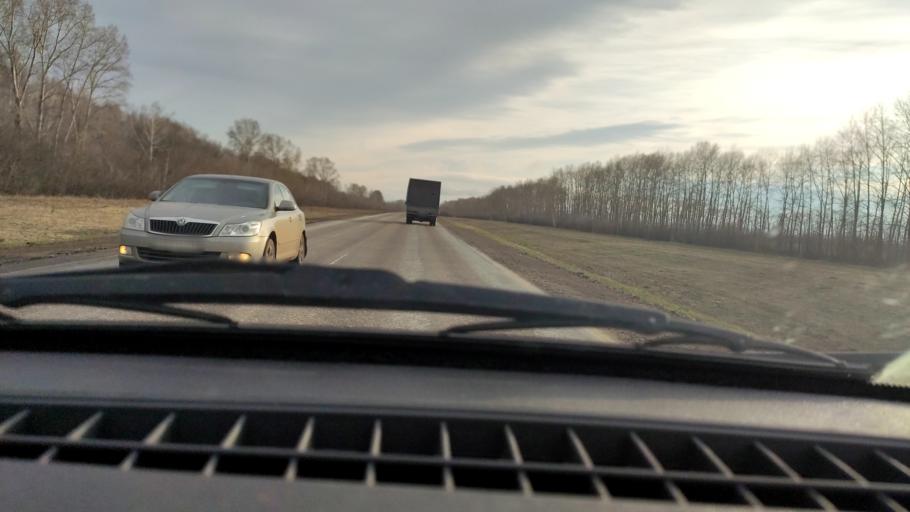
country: RU
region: Bashkortostan
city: Davlekanovo
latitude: 54.3570
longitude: 55.1883
